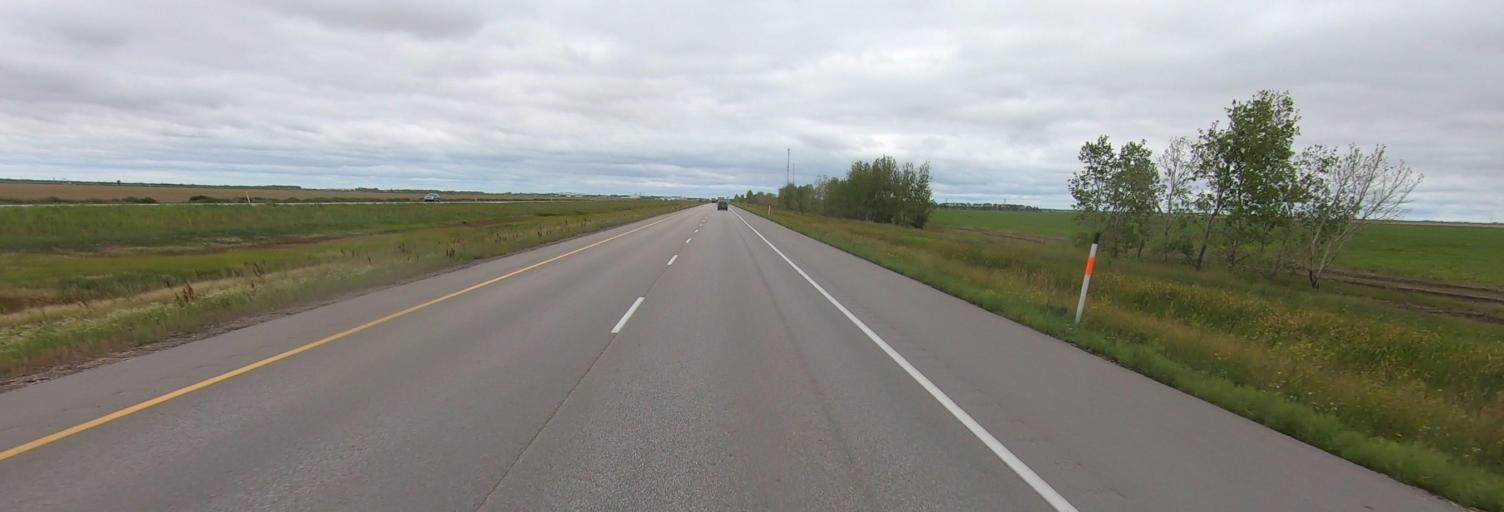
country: CA
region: Manitoba
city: Headingley
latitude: 49.8951
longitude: -97.6936
